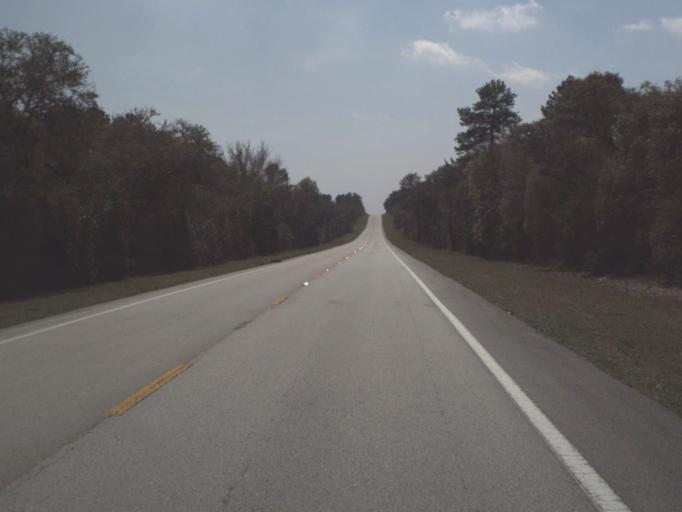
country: US
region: Florida
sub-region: Lake County
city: Astor
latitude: 29.1823
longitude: -81.6517
